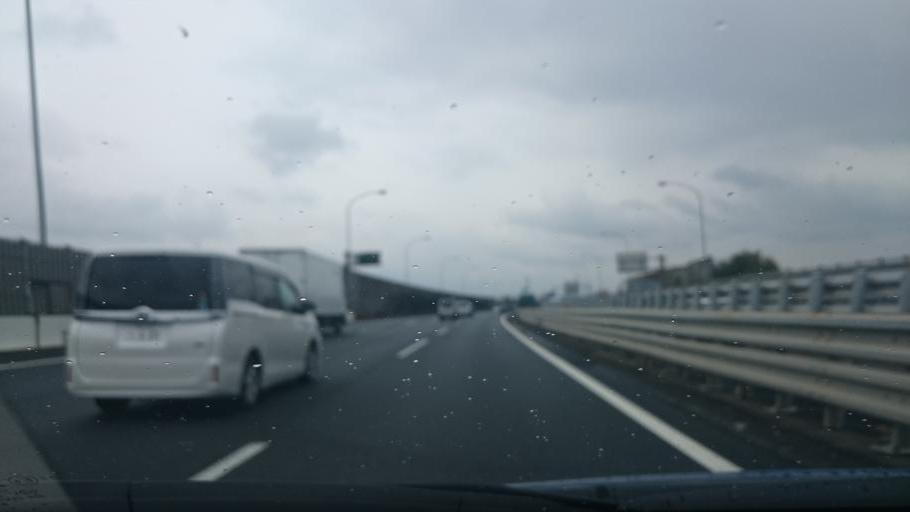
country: JP
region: Saitama
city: Sakado
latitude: 35.9533
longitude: 139.3868
